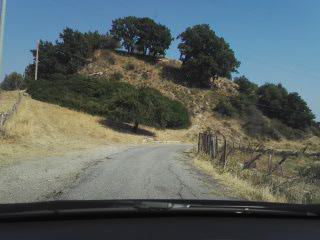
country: IT
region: Calabria
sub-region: Provincia di Reggio Calabria
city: Camini
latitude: 38.4484
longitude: 16.4657
